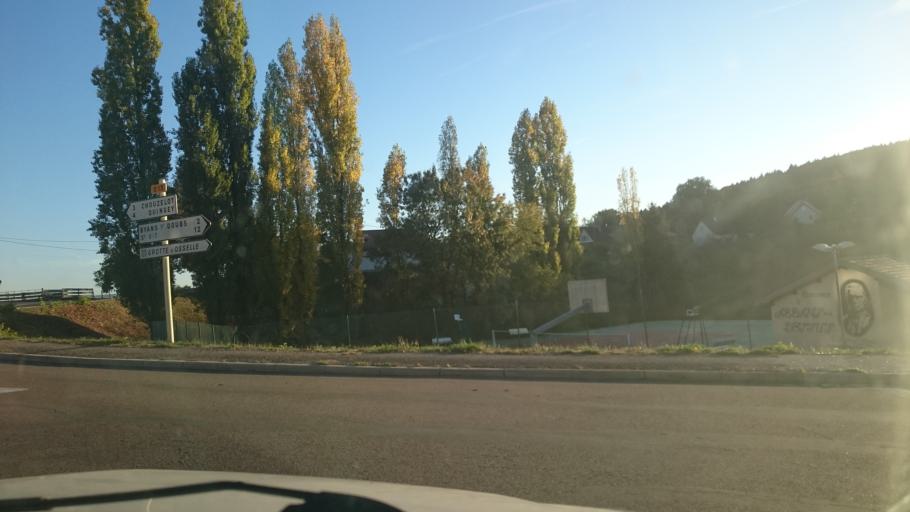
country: FR
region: Franche-Comte
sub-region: Departement du Doubs
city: Quingey
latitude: 47.1143
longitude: 5.8764
